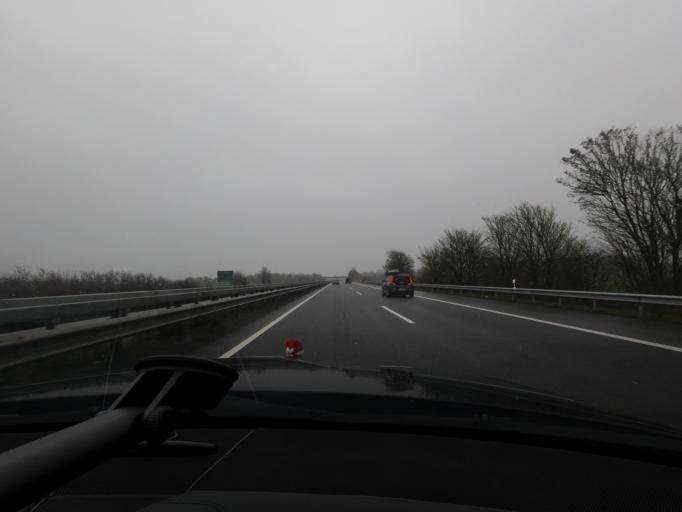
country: DE
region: Schleswig-Holstein
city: Hassmoor
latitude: 54.2637
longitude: 9.7930
